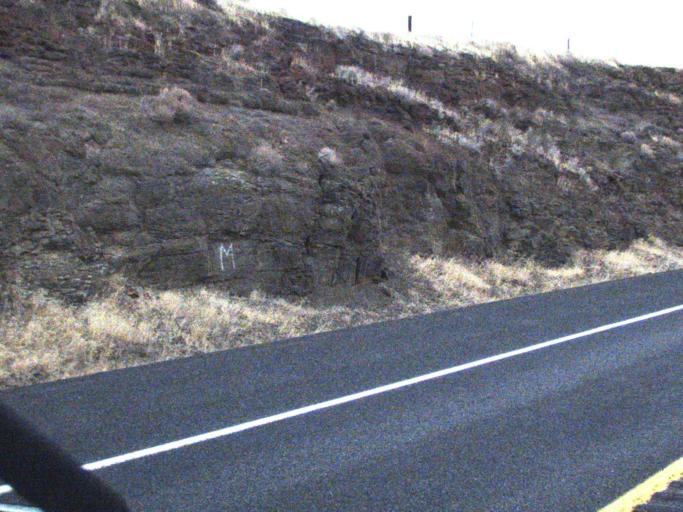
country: US
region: Washington
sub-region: Adams County
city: Ritzville
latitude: 46.7564
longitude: -118.2908
